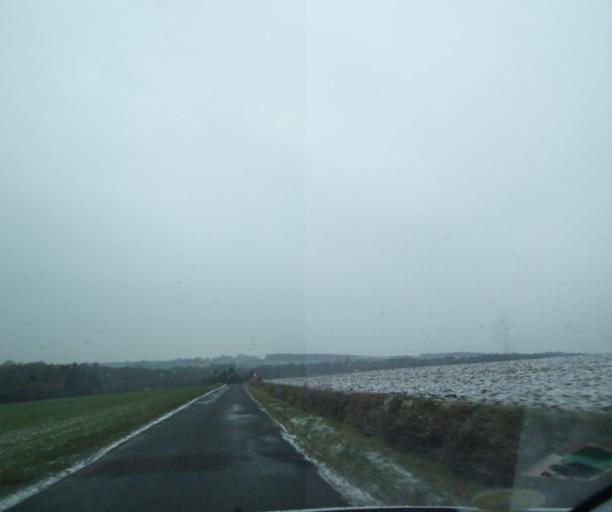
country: FR
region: Champagne-Ardenne
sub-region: Departement de la Haute-Marne
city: Chevillon
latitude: 48.4859
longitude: 5.0519
